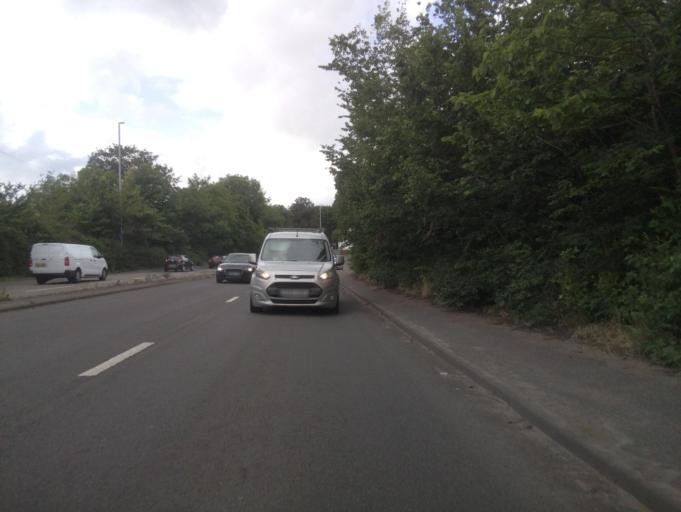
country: GB
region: England
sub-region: Dudley
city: Kingswinford
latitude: 52.4603
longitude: -2.2051
